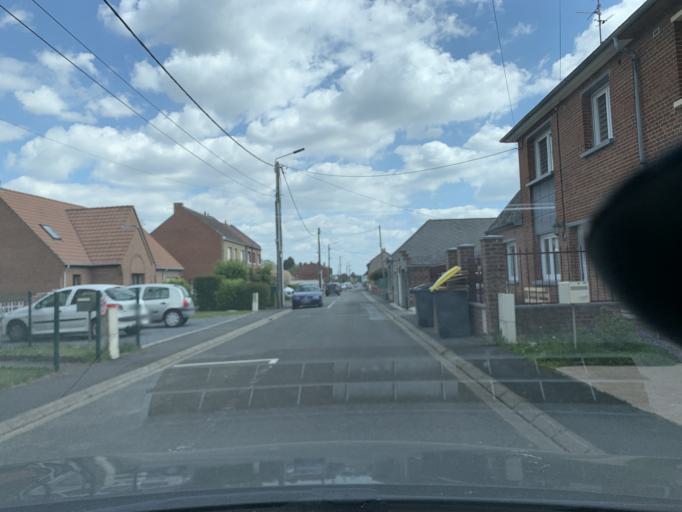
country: FR
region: Nord-Pas-de-Calais
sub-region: Departement du Pas-de-Calais
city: Ecourt-Saint-Quentin
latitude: 50.2524
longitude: 3.0729
